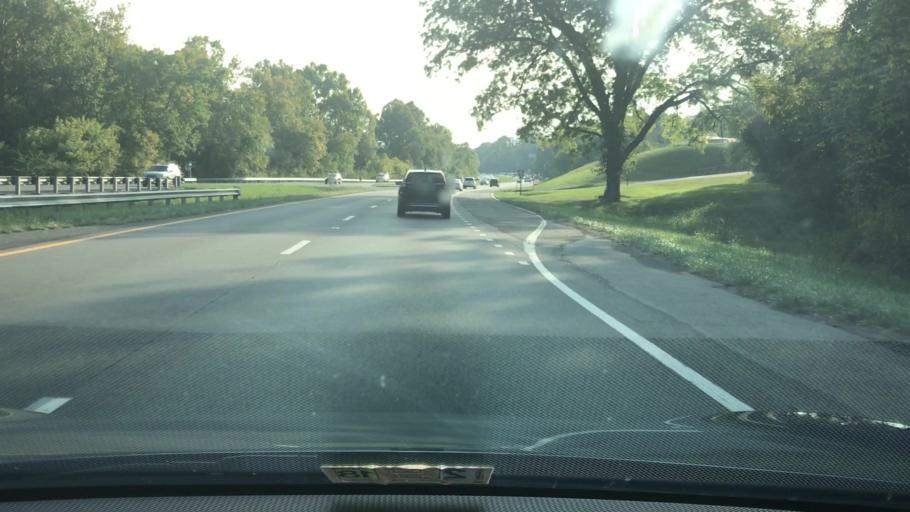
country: US
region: Virginia
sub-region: Botetourt County
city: Laymantown
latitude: 37.3399
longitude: -79.8519
